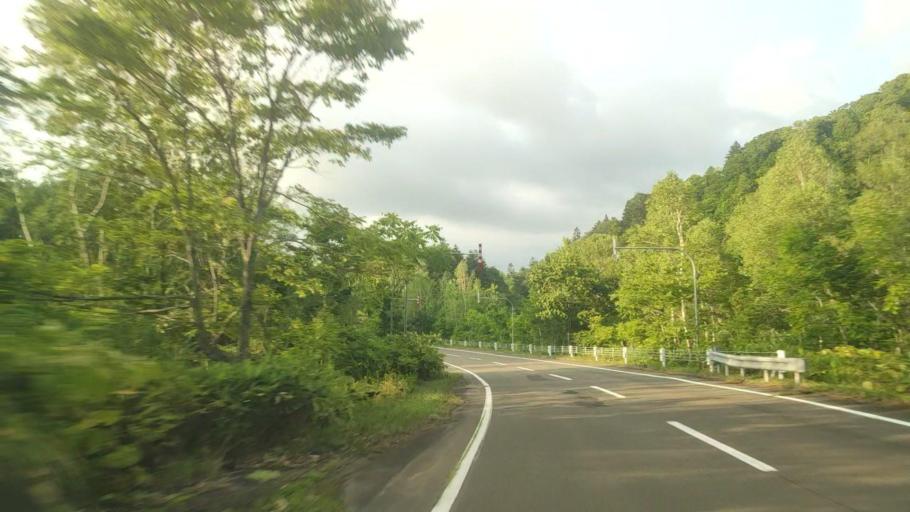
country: JP
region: Hokkaido
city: Bibai
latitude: 43.1375
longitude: 142.0968
